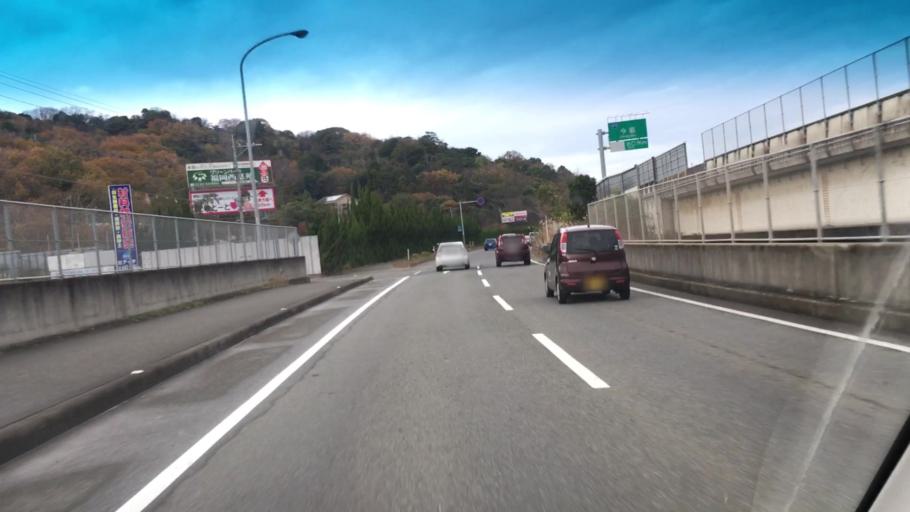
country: JP
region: Fukuoka
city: Maebaru-chuo
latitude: 33.5695
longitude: 130.2911
